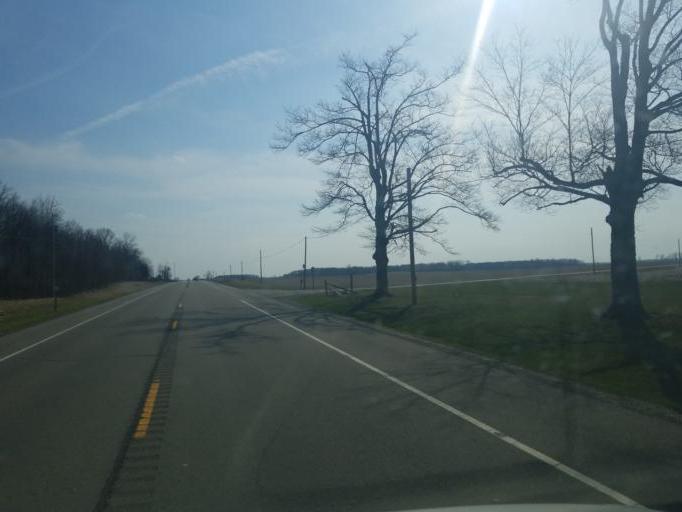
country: US
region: Ohio
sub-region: Logan County
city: Northwood
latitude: 40.5339
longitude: -83.6777
